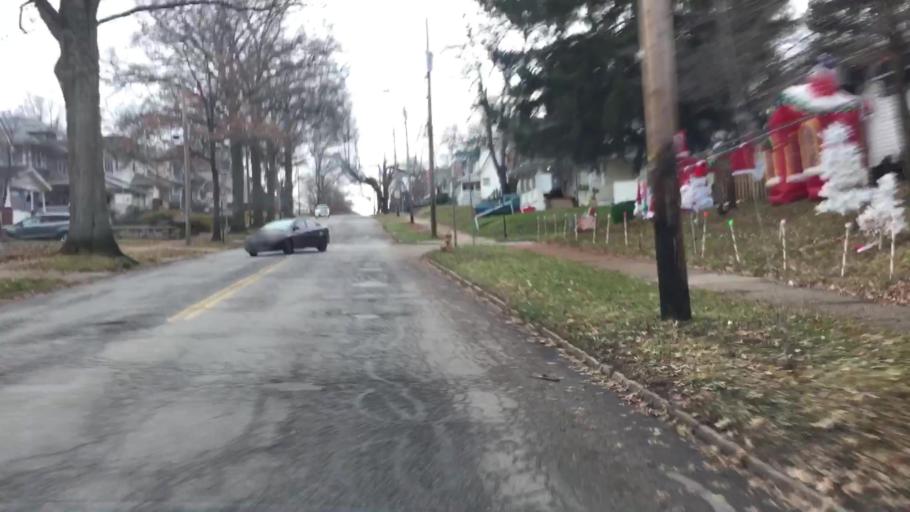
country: US
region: Ohio
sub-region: Summit County
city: Tallmadge
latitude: 41.0812
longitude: -81.4720
